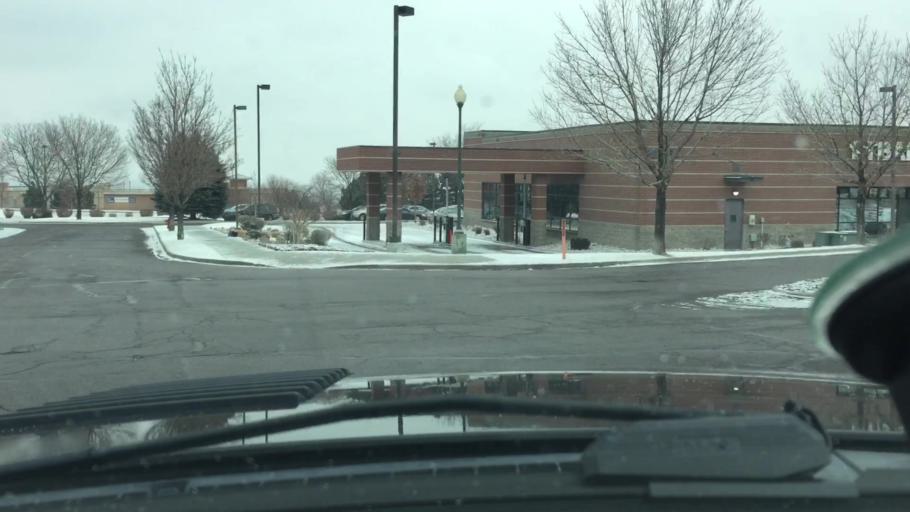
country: US
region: Colorado
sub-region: Adams County
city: Northglenn
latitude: 39.8835
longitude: -105.0261
